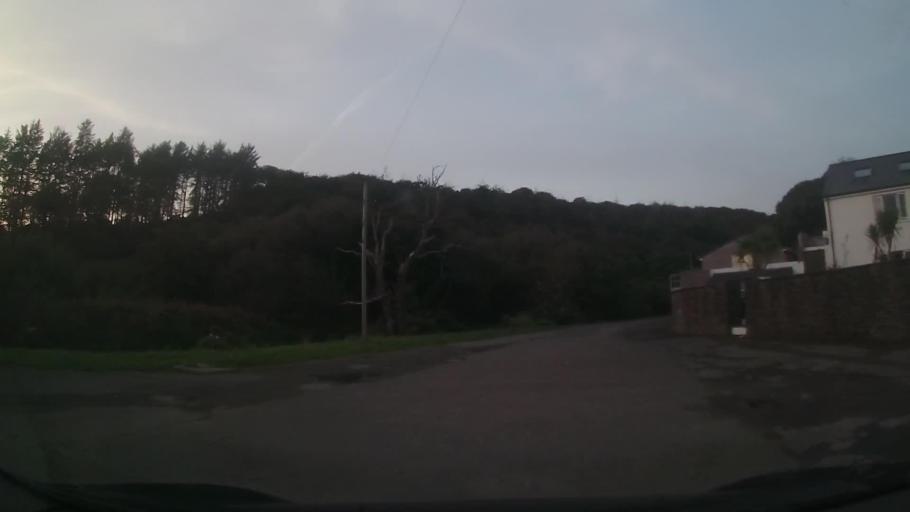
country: GB
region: Wales
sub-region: Pembrokeshire
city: Saundersfoot
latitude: 51.7343
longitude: -4.6480
